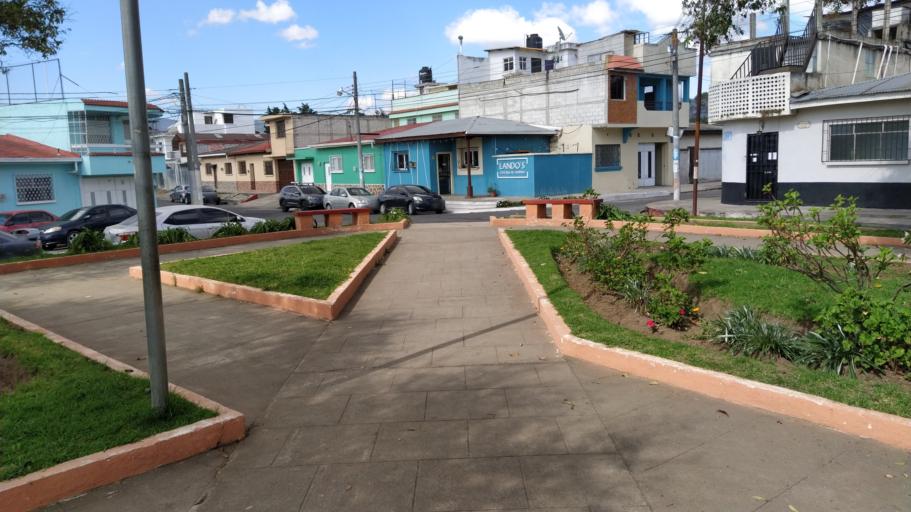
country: GT
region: Quetzaltenango
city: Quetzaltenango
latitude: 14.8455
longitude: -91.5126
